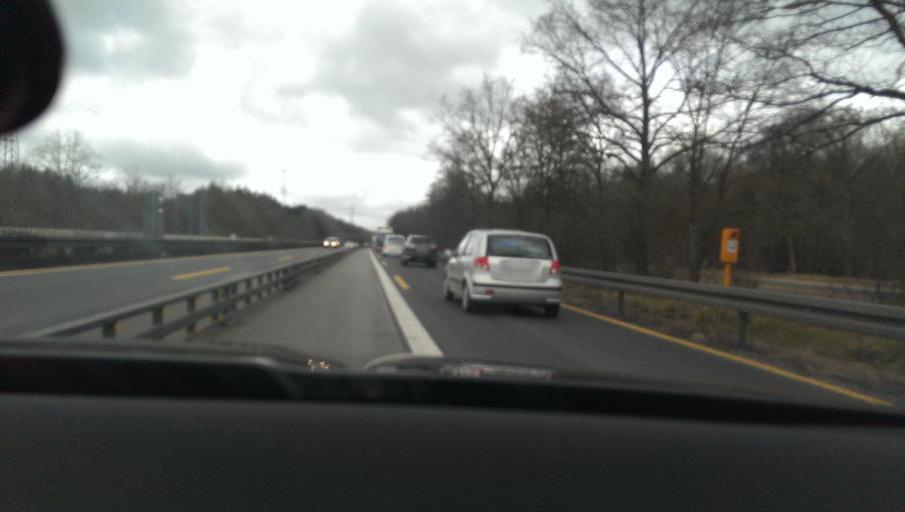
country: DE
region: Hesse
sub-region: Regierungsbezirk Kassel
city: Petersberg
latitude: 50.5881
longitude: 9.6970
